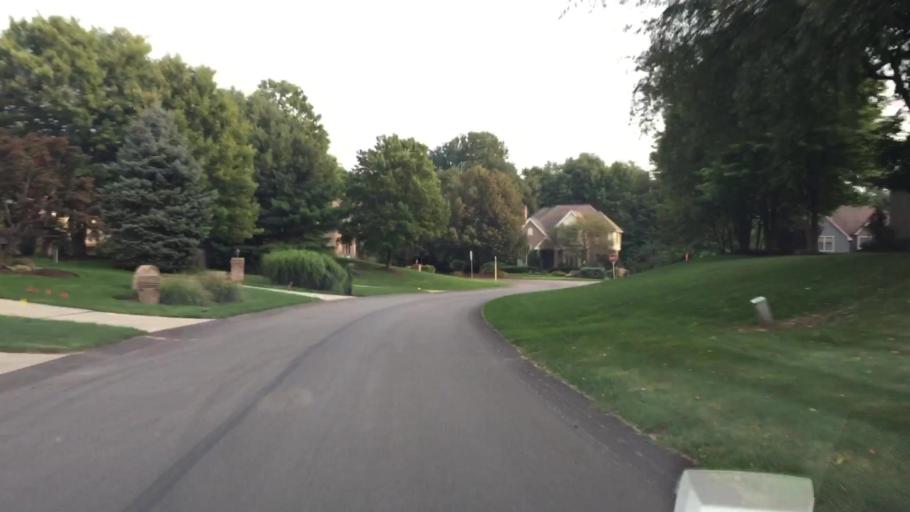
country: US
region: Pennsylvania
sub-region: Allegheny County
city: Bradford Woods
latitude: 40.6452
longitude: -80.1108
